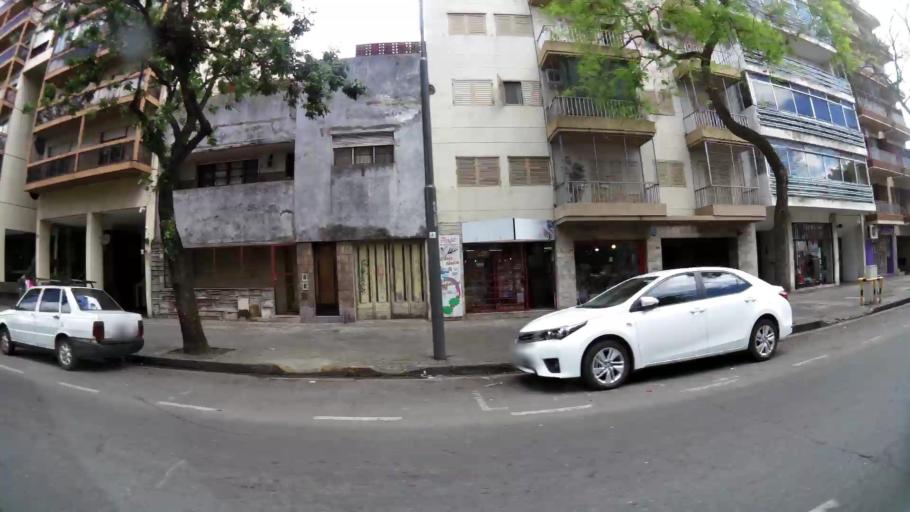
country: AR
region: Santa Fe
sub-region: Departamento de Rosario
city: Rosario
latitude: -32.9583
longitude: -60.6350
